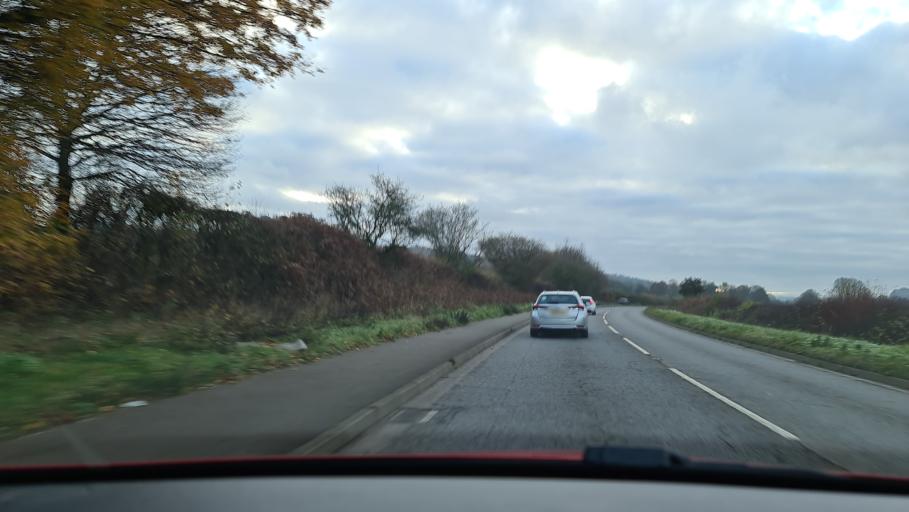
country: GB
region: England
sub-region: Buckinghamshire
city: Princes Risborough
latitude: 51.6705
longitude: -0.8145
